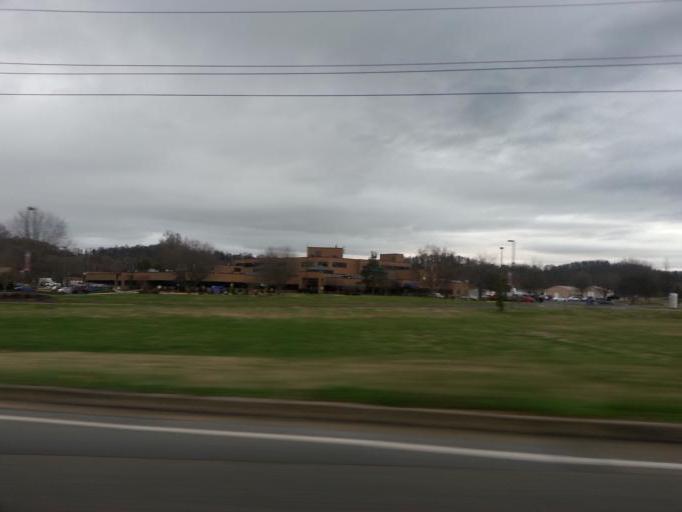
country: US
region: Tennessee
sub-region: Carter County
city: Elizabethton
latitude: 36.3447
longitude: -82.2483
